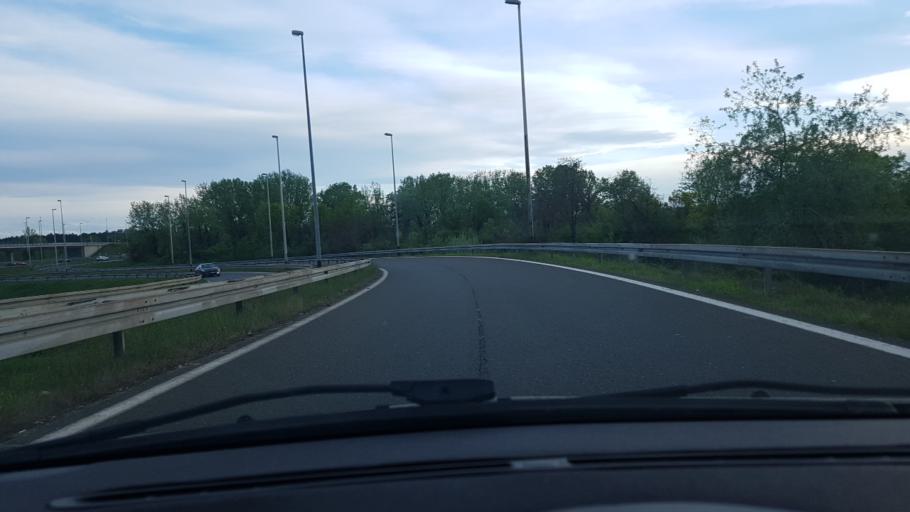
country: HR
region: Grad Zagreb
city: Jezdovec
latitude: 45.7901
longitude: 15.8464
